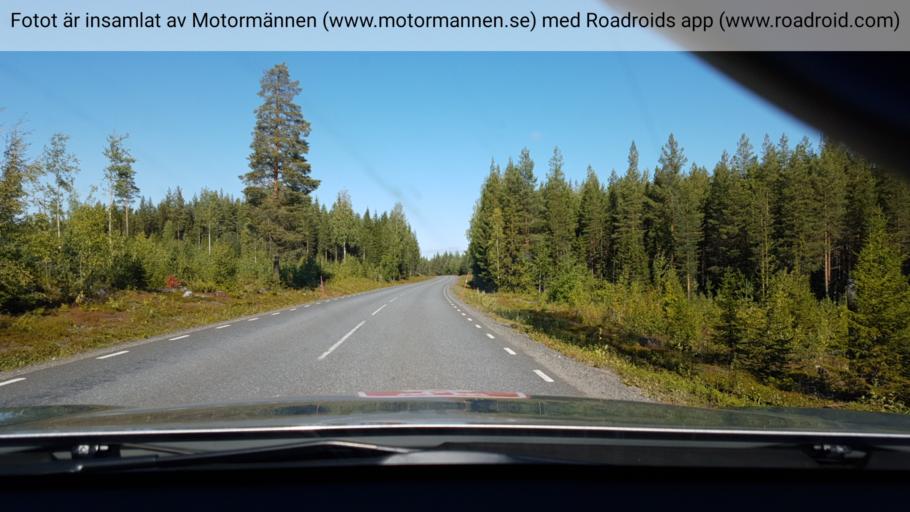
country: SE
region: Vaesterbotten
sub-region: Norsjo Kommun
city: Norsjoe
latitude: 64.9919
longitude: 19.4310
